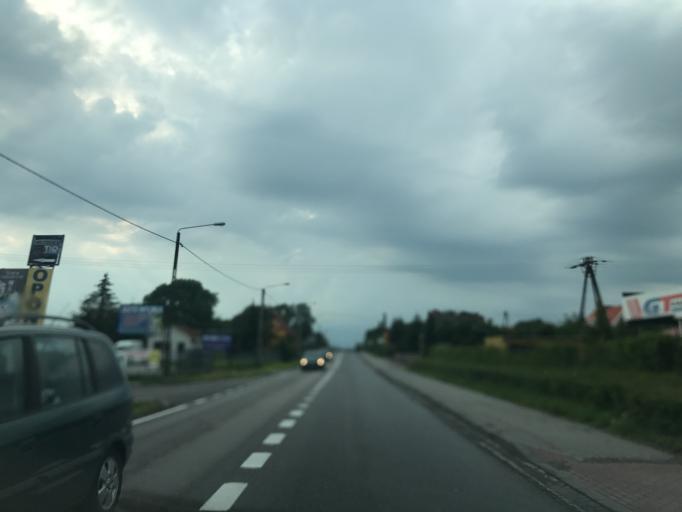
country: PL
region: Pomeranian Voivodeship
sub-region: Powiat czluchowski
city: Czluchow
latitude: 53.6731
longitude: 17.3477
